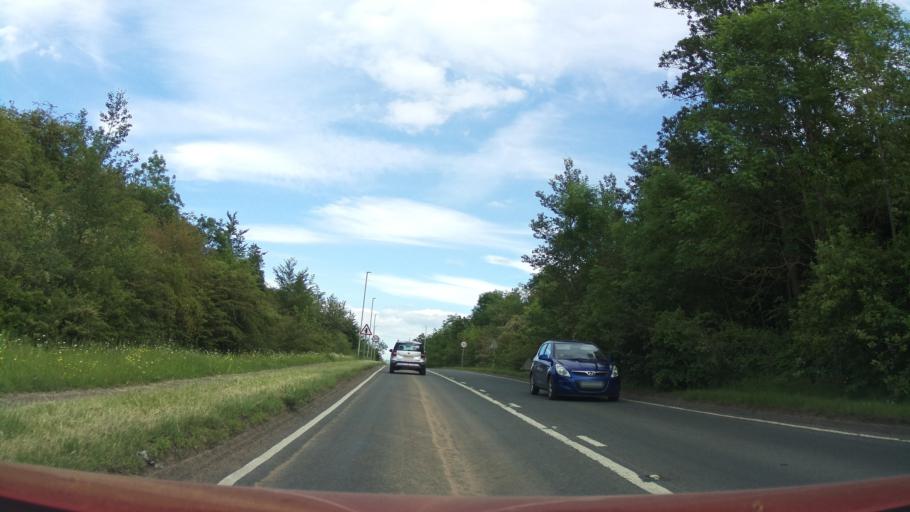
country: GB
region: England
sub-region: Worcestershire
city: Evesham
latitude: 52.0892
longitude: -1.9738
